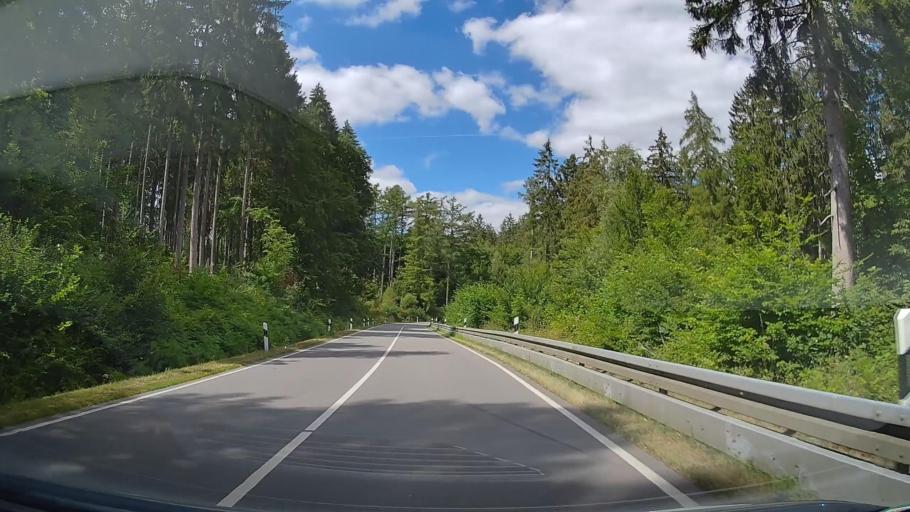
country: DE
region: Lower Saxony
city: Belm
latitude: 52.3602
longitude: 8.1406
